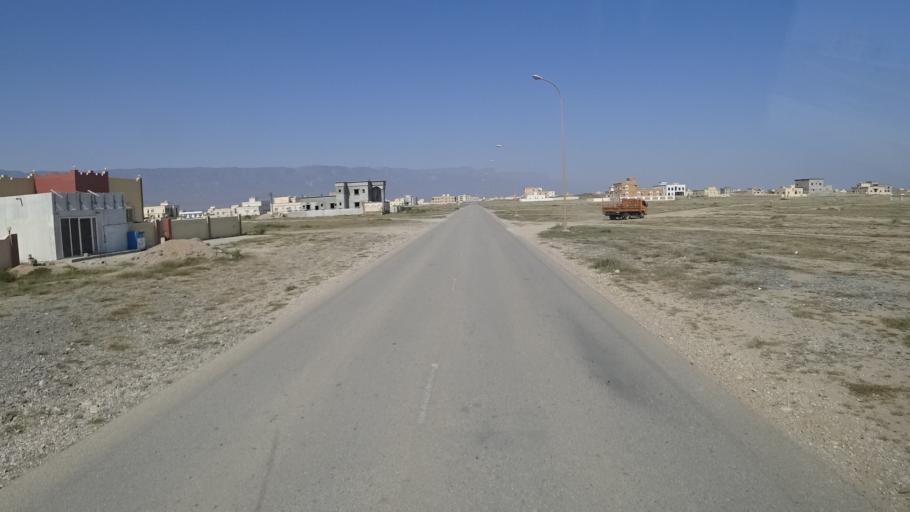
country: OM
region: Zufar
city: Salalah
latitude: 16.9868
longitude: 54.7142
